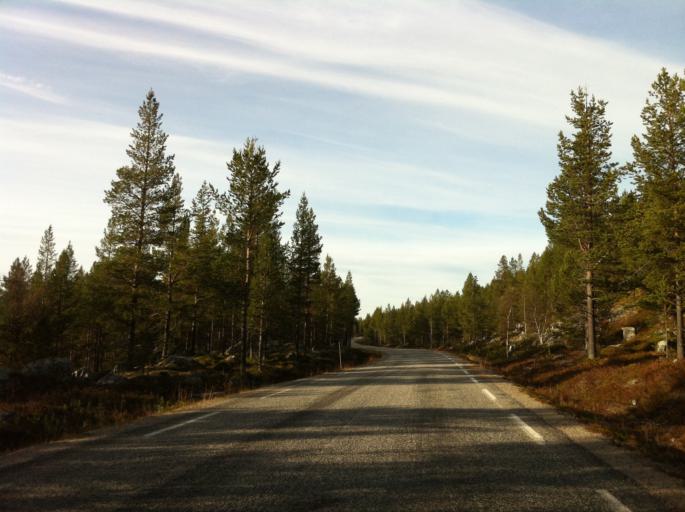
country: NO
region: Hedmark
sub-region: Engerdal
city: Engerdal
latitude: 62.1227
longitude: 12.0051
